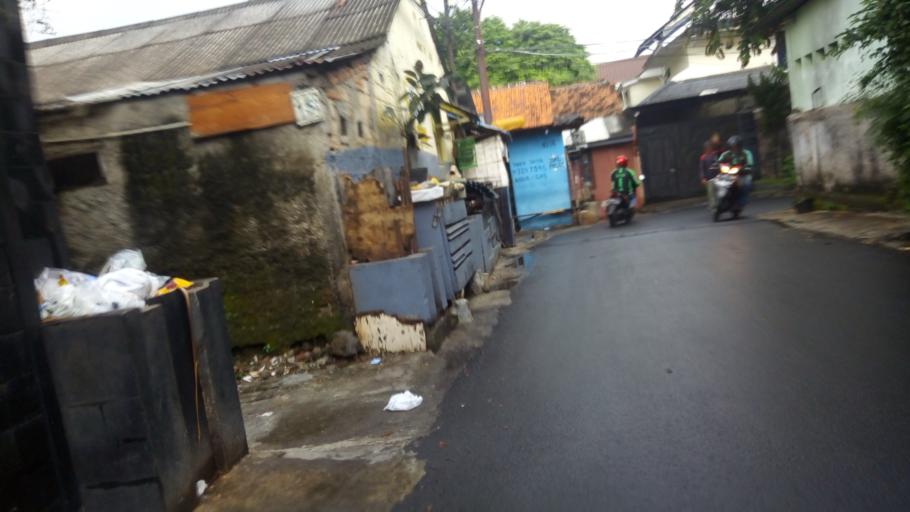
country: ID
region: Jakarta Raya
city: Jakarta
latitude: -6.2652
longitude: 106.8071
